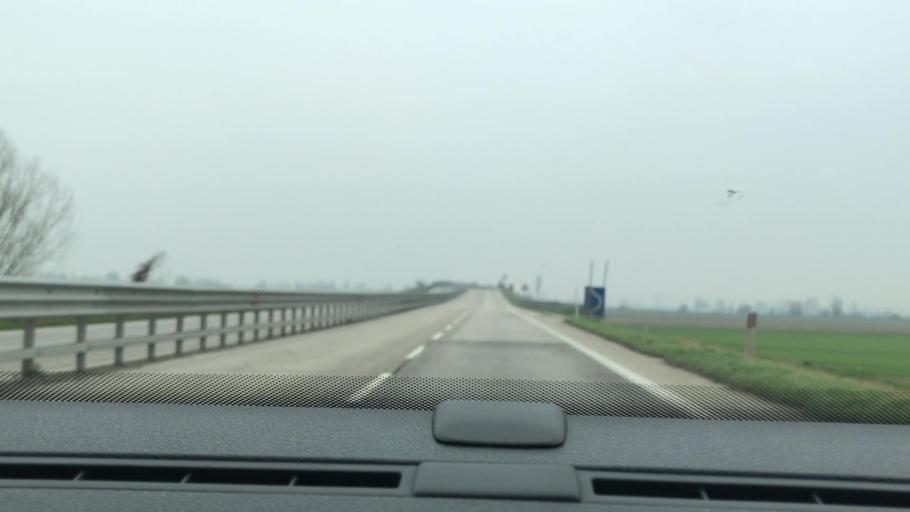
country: IT
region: Veneto
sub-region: Provincia di Rovigo
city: Grignano Polesine
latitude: 45.0252
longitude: 11.7526
